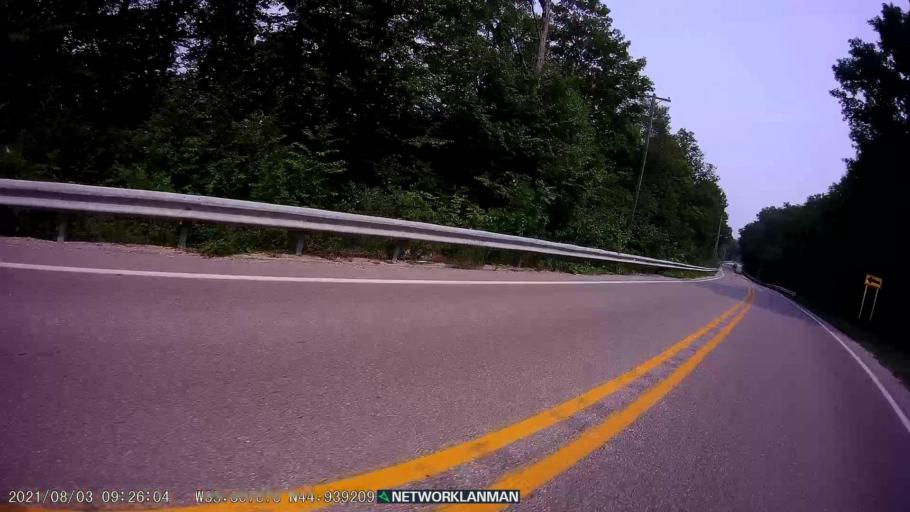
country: US
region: Michigan
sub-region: Leelanau County
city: Leland
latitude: 44.9398
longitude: -85.8072
